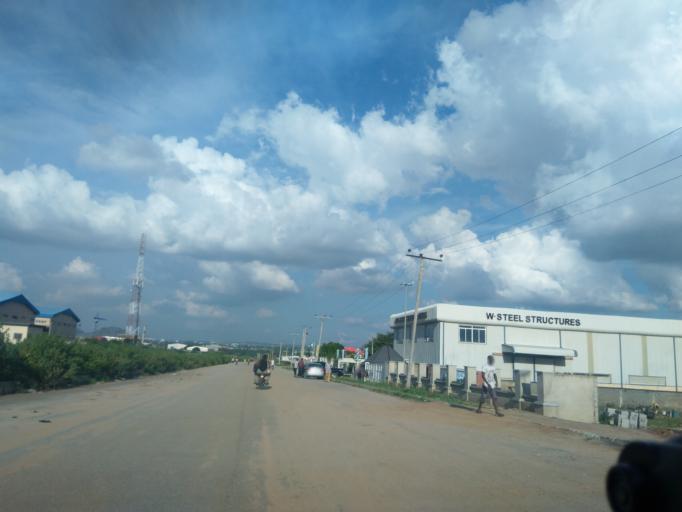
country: NG
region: Abuja Federal Capital Territory
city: Abuja
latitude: 9.0296
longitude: 7.4014
